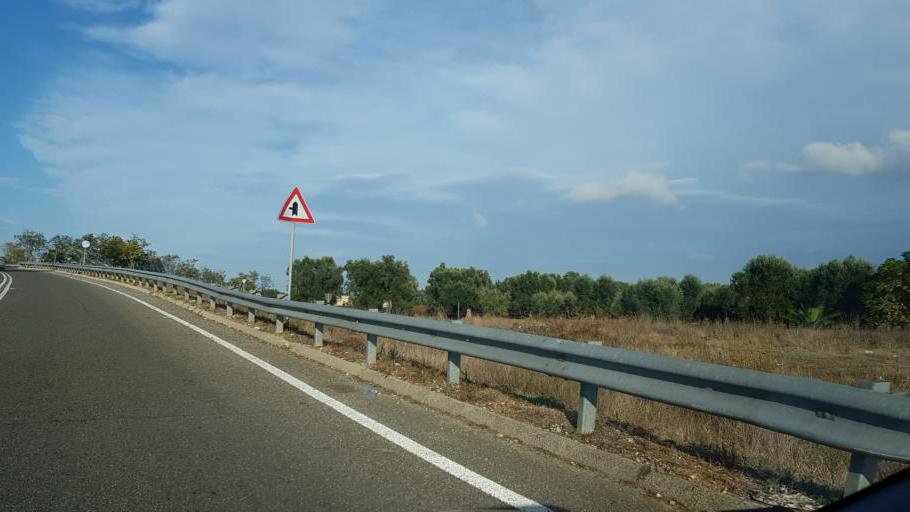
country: IT
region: Apulia
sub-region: Provincia di Brindisi
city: Oria
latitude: 40.5370
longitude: 17.6549
